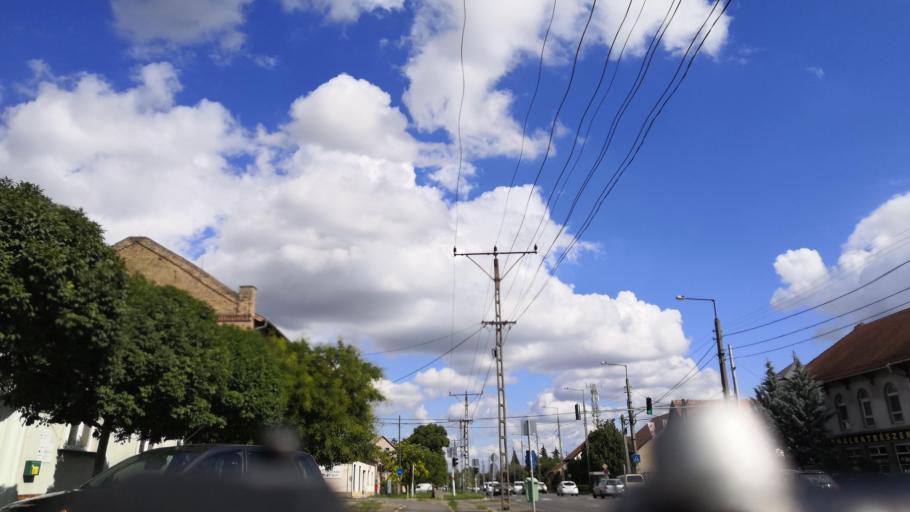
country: HU
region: Csongrad
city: Domaszek
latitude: 46.2731
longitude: 20.0704
